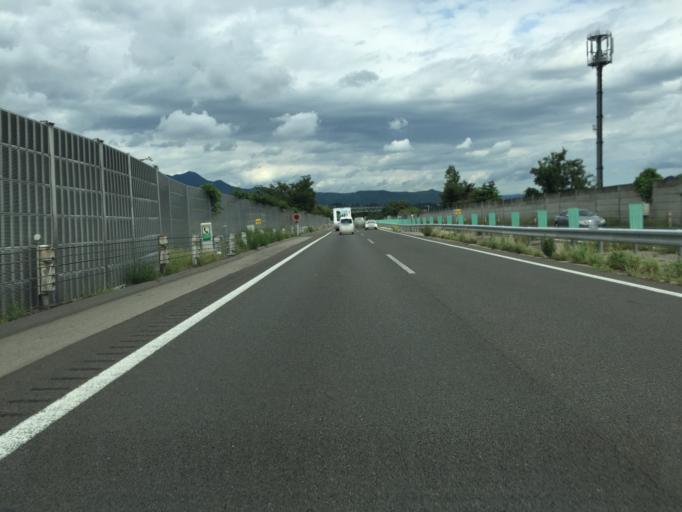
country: JP
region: Miyagi
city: Shiroishi
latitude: 37.9932
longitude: 140.6072
